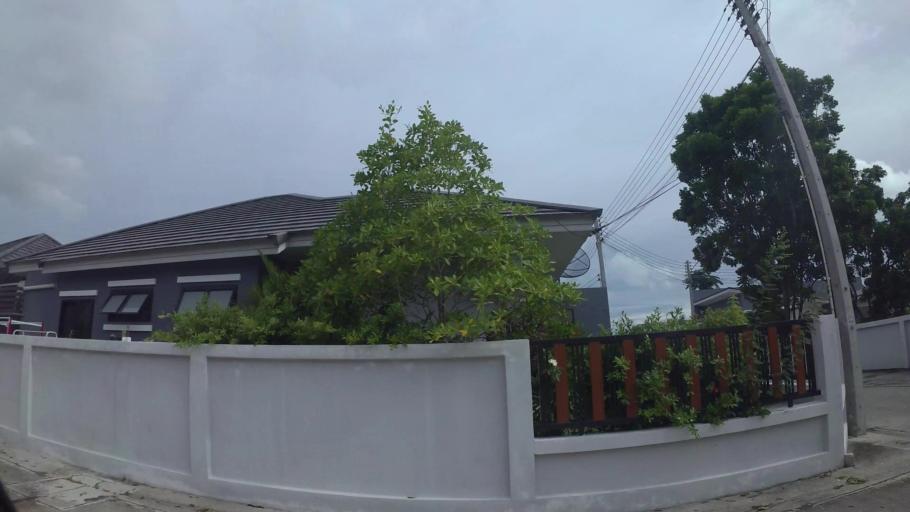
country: TH
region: Rayong
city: Rayong
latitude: 12.6649
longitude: 101.2810
